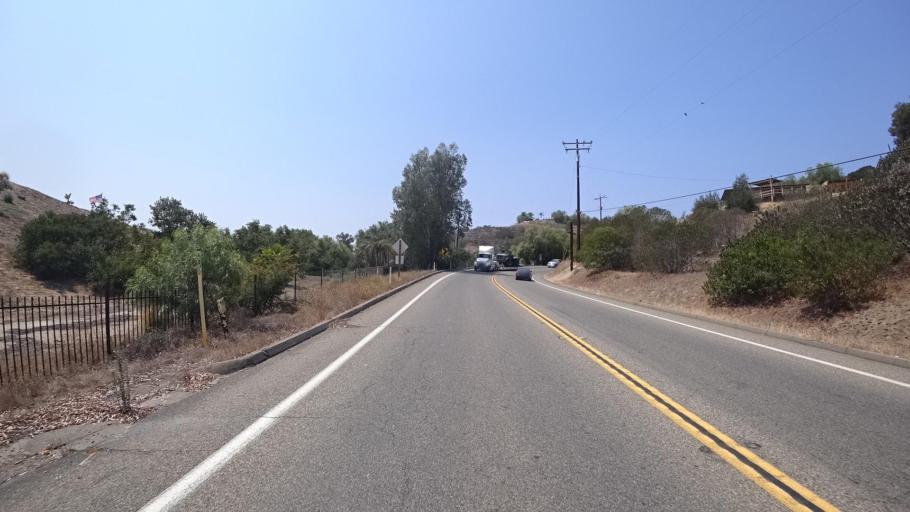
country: US
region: California
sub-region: San Diego County
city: Rainbow
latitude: 33.3898
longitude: -117.1811
